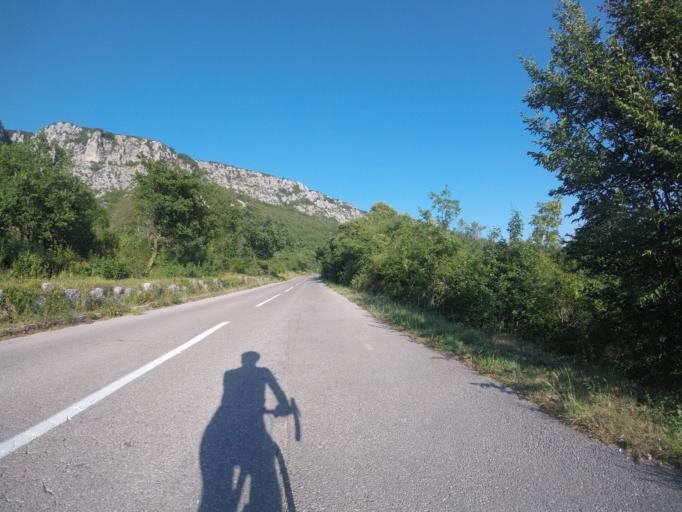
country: HR
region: Primorsko-Goranska
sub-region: Grad Crikvenica
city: Crikvenica
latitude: 45.2118
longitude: 14.7088
